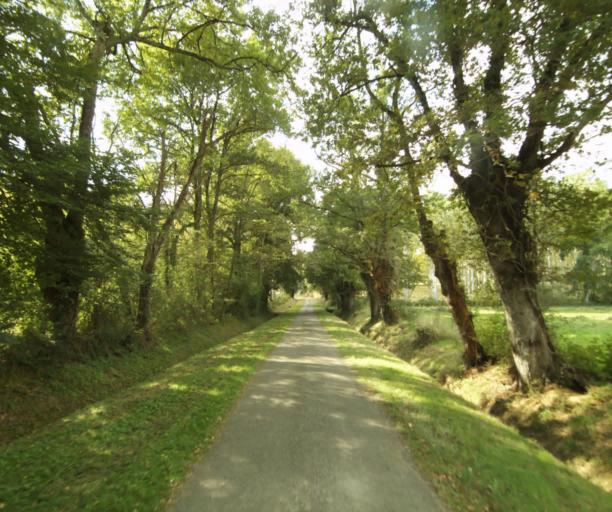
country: FR
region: Midi-Pyrenees
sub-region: Departement du Gers
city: Cazaubon
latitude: 43.8846
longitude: -0.0480
